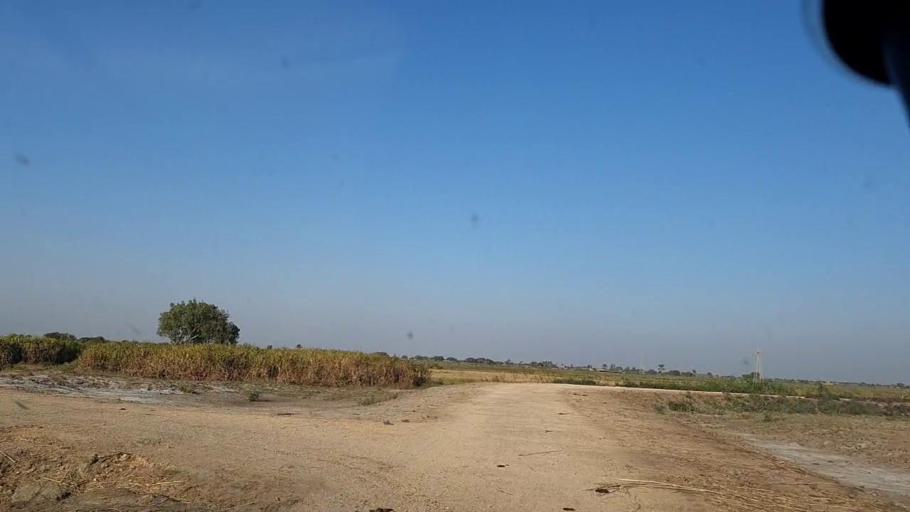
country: PK
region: Sindh
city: Chuhar Jamali
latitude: 24.5617
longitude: 68.0722
